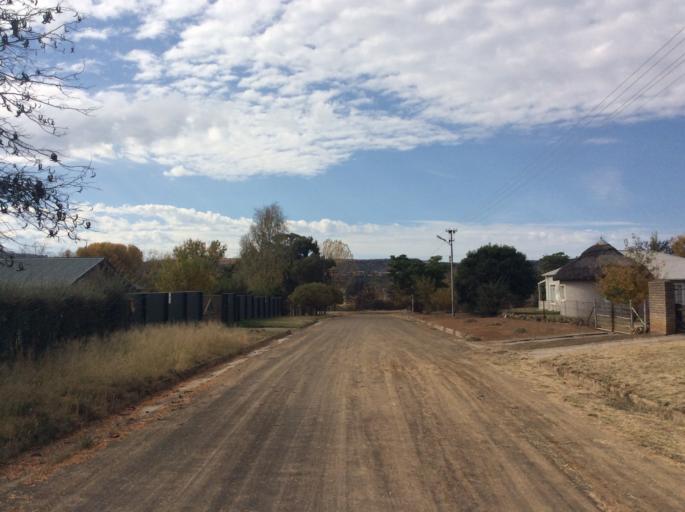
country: LS
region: Mafeteng
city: Mafeteng
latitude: -29.7301
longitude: 27.0311
